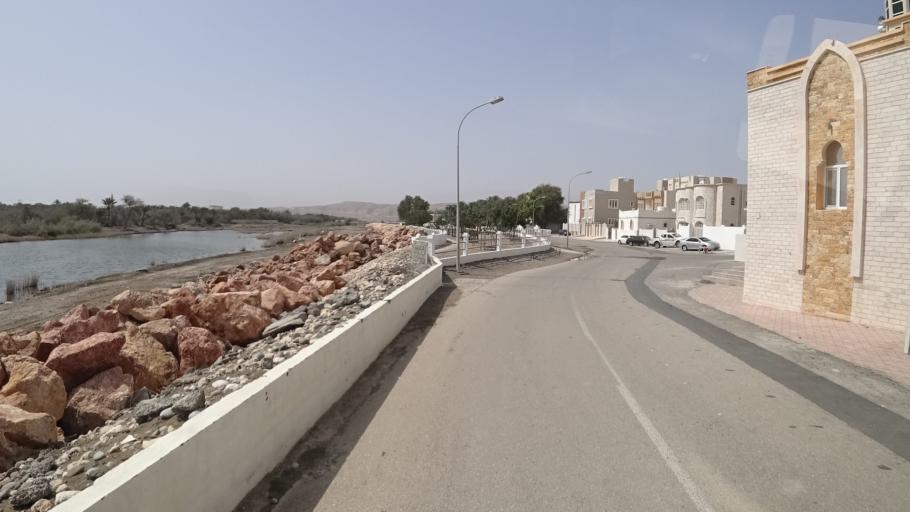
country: OM
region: Muhafazat Masqat
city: Muscat
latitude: 23.2162
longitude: 58.9743
